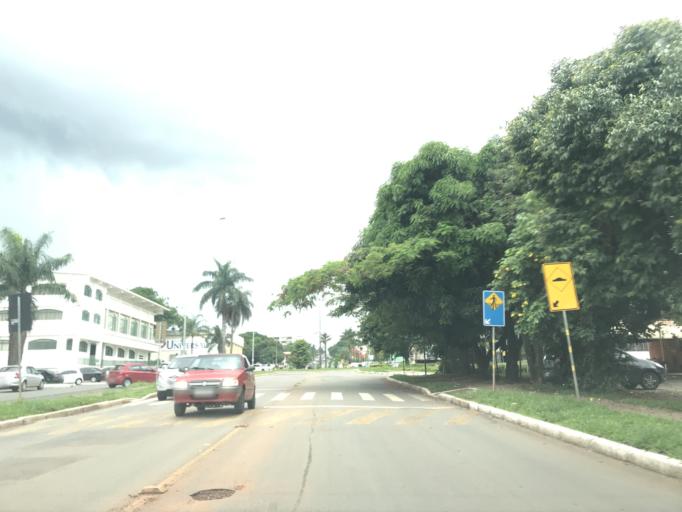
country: BR
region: Federal District
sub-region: Brasilia
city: Brasilia
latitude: -15.6474
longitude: -47.8044
